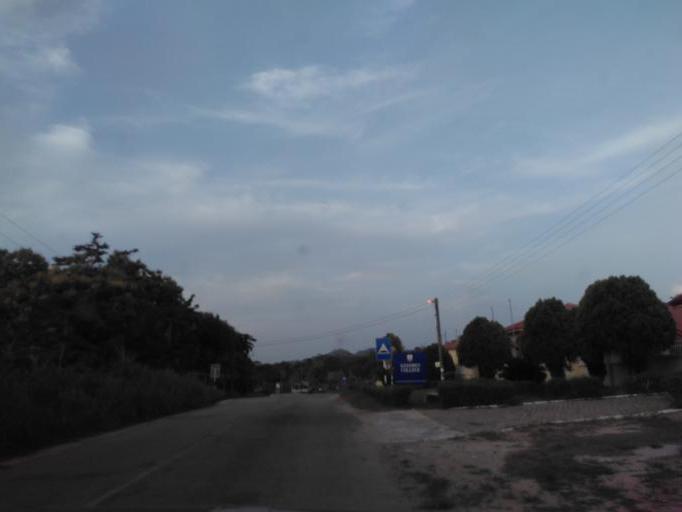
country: GH
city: Bekwai
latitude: 6.5413
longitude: -1.4517
